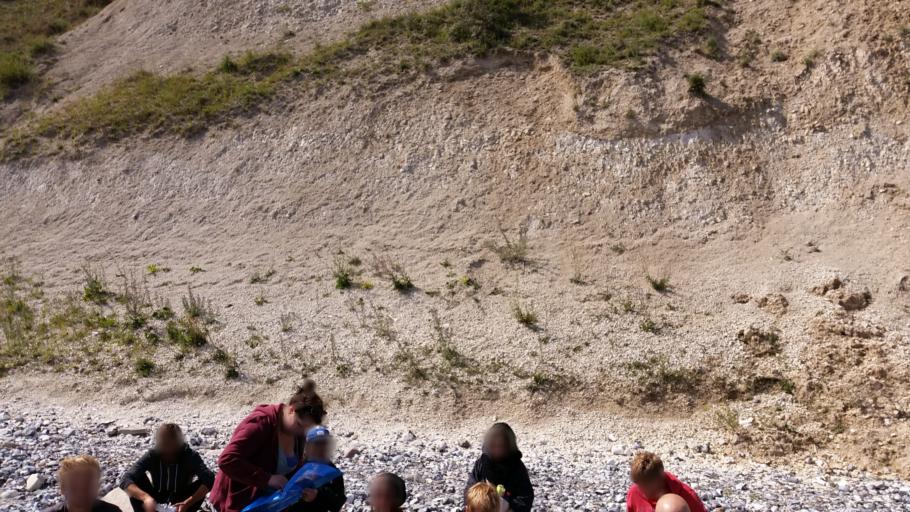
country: DE
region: Mecklenburg-Vorpommern
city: Altenkirchen
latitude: 54.6756
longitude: 13.4367
